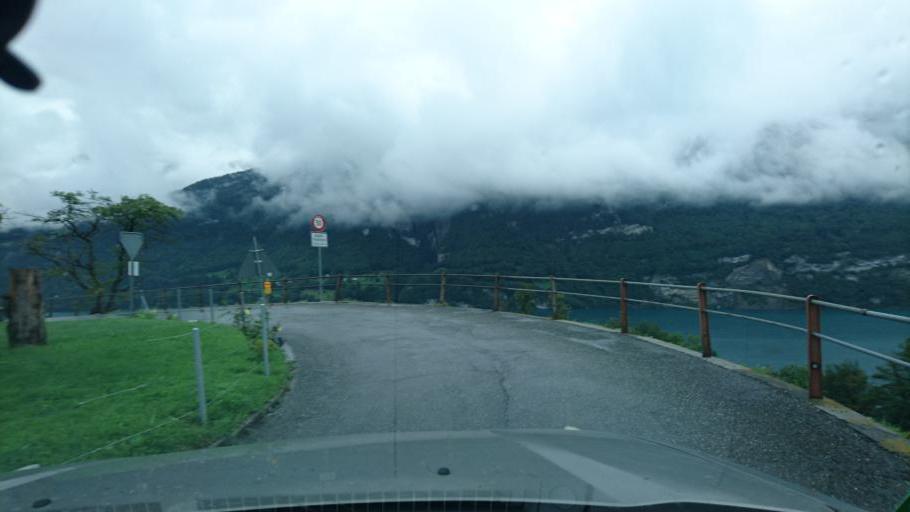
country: CH
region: Saint Gallen
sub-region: Wahlkreis See-Gaster
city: Amden
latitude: 47.1169
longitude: 9.1656
